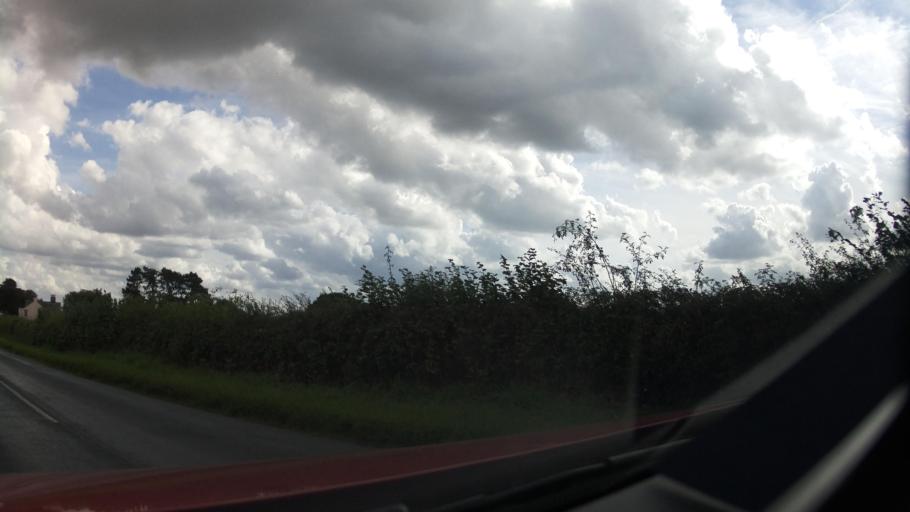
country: GB
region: England
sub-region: North Yorkshire
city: Bedale
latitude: 54.2423
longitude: -1.6873
